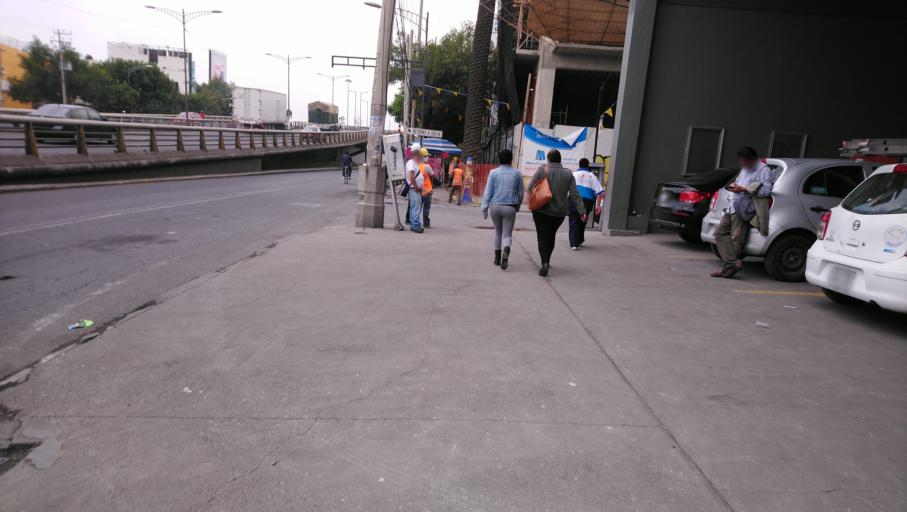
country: MX
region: Mexico City
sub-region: Iztacalco
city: Iztacalco
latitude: 19.4037
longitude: -99.1136
